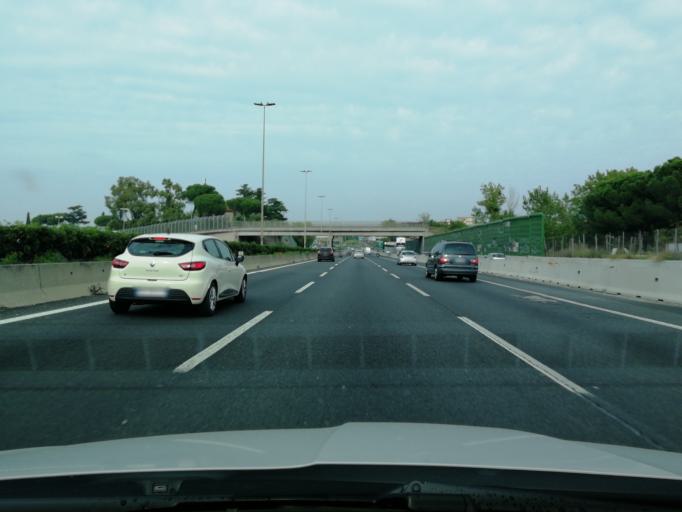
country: IT
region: Latium
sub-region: Citta metropolitana di Roma Capitale
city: Setteville
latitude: 41.8846
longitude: 12.6124
